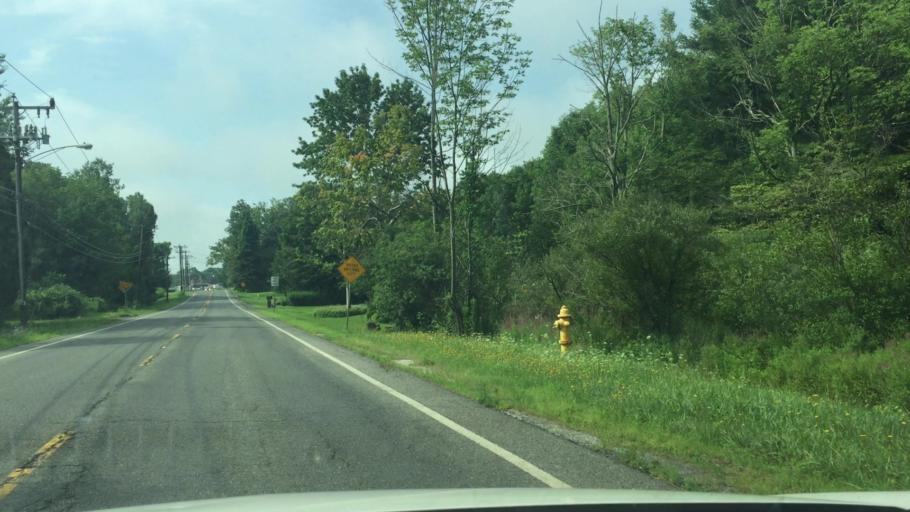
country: US
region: Massachusetts
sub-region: Berkshire County
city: Richmond
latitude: 42.4227
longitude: -73.3344
